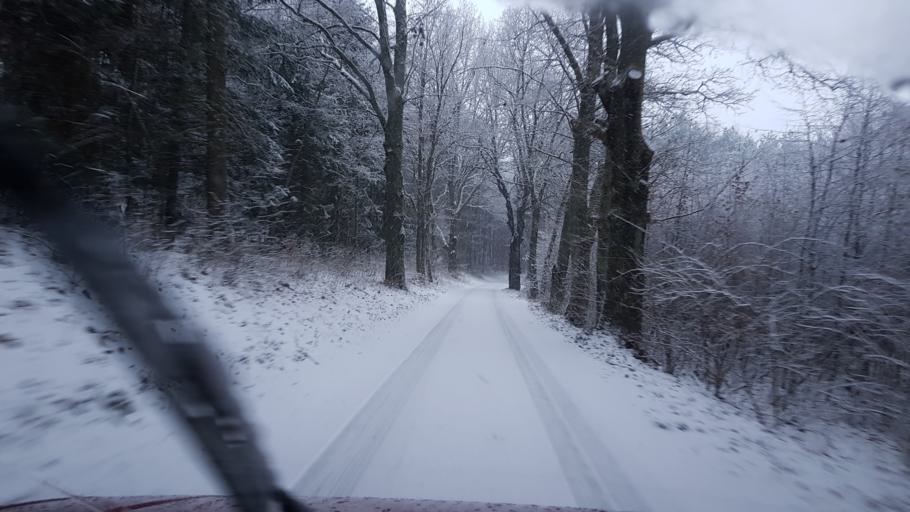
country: PL
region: West Pomeranian Voivodeship
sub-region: Powiat koszalinski
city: Polanow
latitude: 54.2355
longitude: 16.6305
